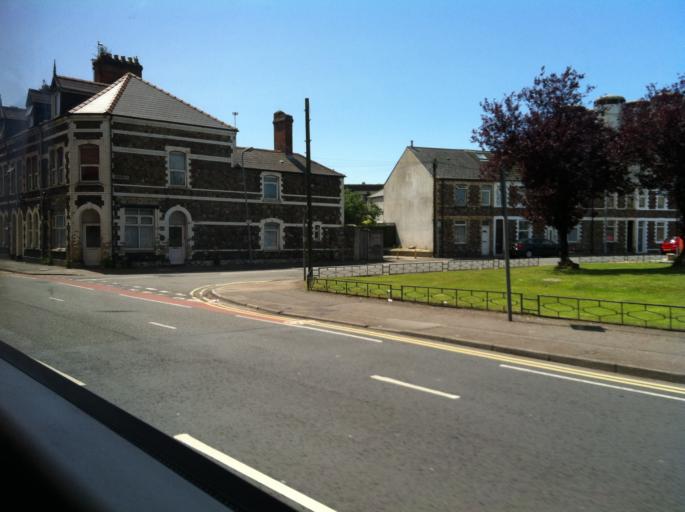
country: GB
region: Wales
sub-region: Cardiff
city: Cardiff
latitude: 51.4737
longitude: -3.1784
